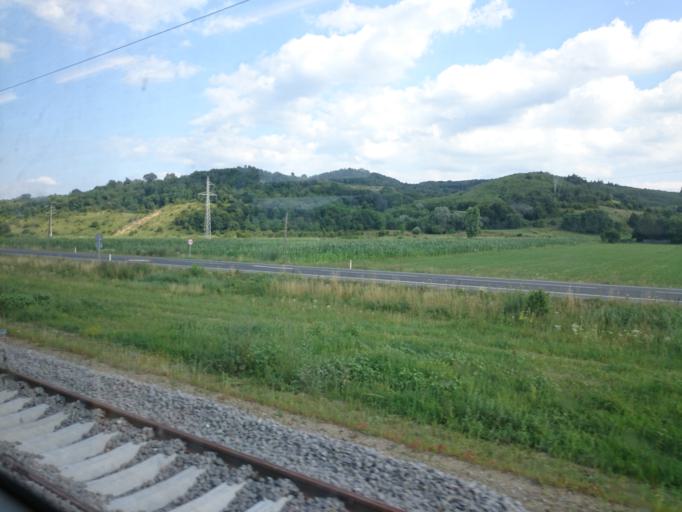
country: RO
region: Sibiu
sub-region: Comuna Hoghilag
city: Hoghilag
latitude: 46.2199
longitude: 24.6041
